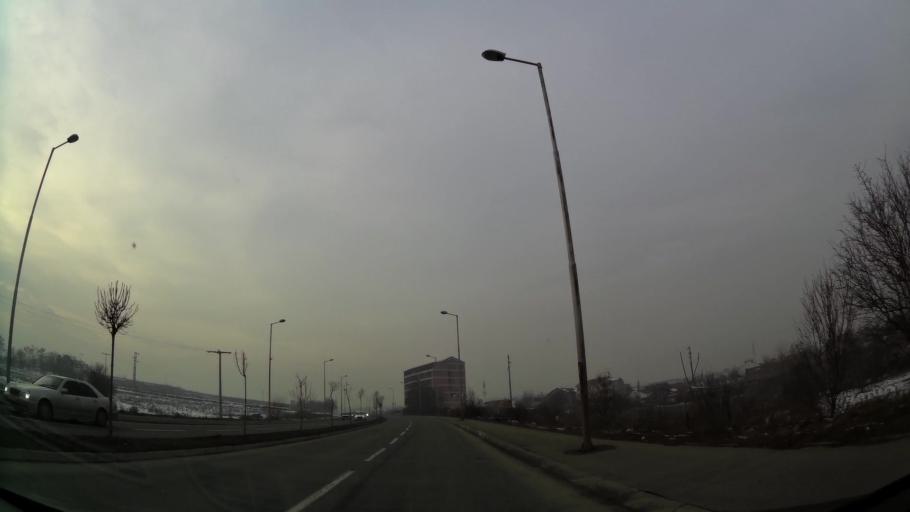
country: MK
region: Suto Orizari
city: Suto Orizare
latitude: 42.0265
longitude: 21.4246
